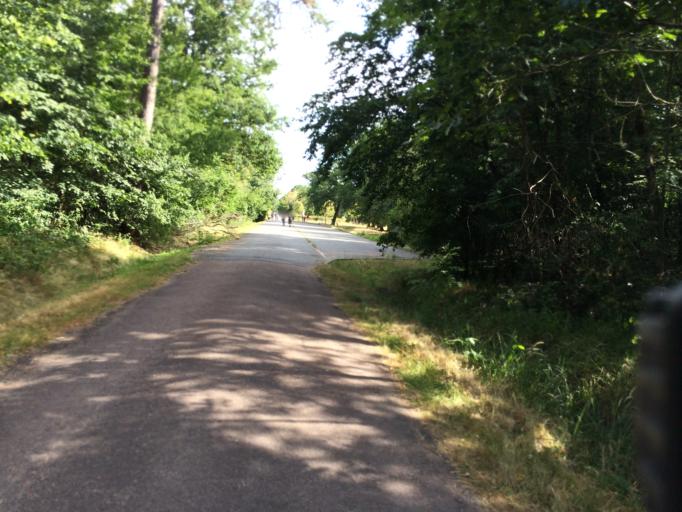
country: FR
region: Ile-de-France
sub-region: Departement de l'Essonne
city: Tigery
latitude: 48.6583
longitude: 2.4924
